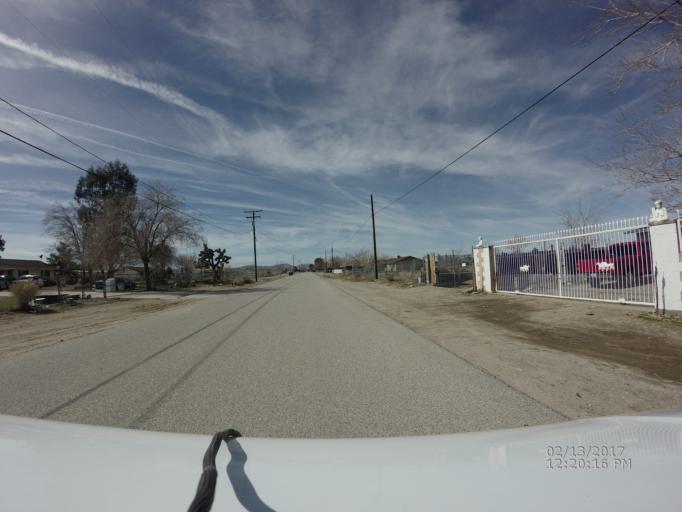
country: US
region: California
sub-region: Los Angeles County
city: Littlerock
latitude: 34.5653
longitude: -117.9258
